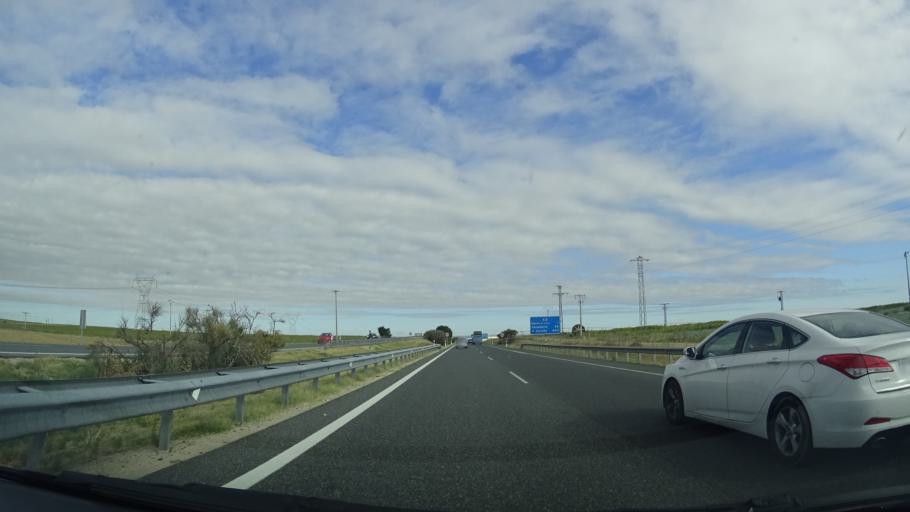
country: ES
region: Castille and Leon
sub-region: Provincia de Valladolid
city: San Vicente del Palacio
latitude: 41.2255
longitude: -4.8475
